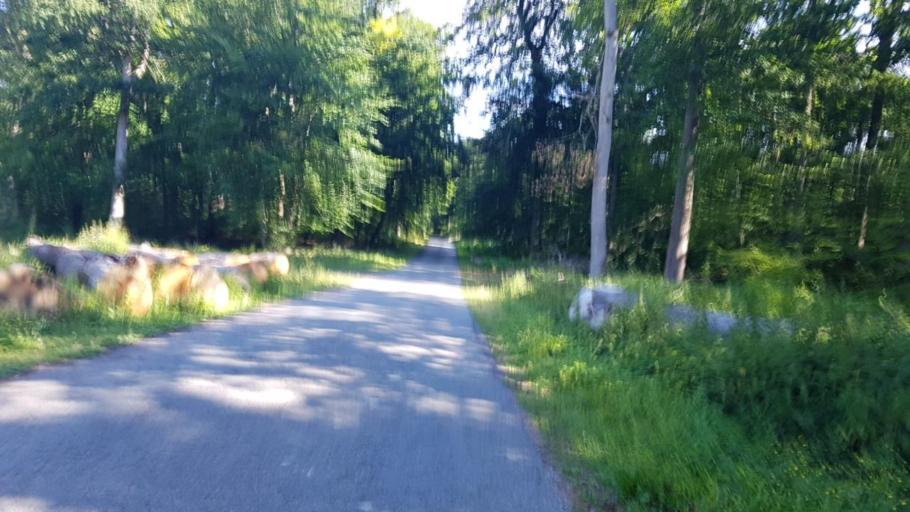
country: FR
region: Picardie
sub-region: Departement de l'Oise
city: Fleurines
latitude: 49.2662
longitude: 2.6175
